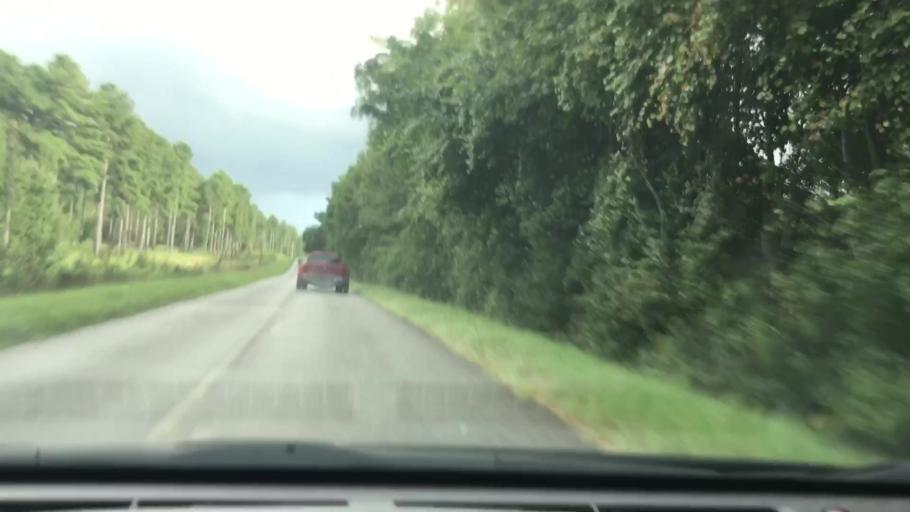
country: US
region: Georgia
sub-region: Jefferson County
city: Wadley
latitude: 32.8111
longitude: -82.3751
